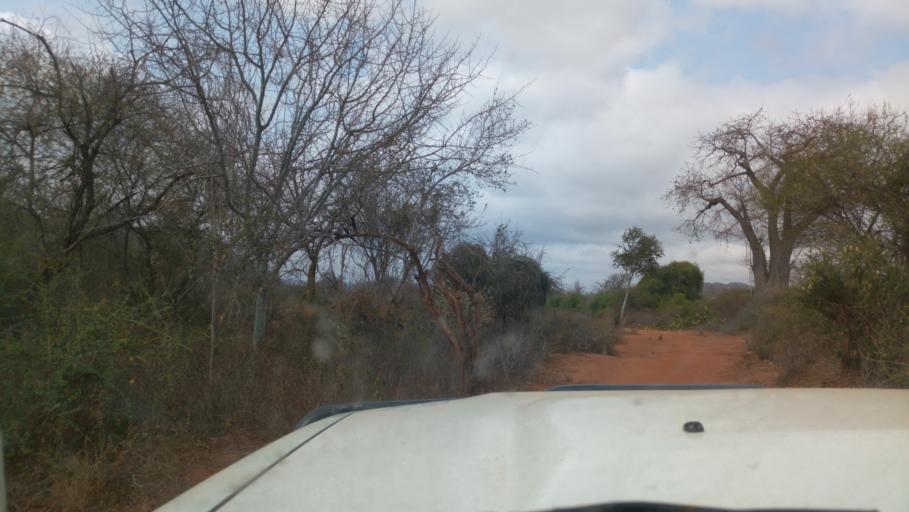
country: KE
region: Kitui
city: Kitui
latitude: -1.8620
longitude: 38.2811
